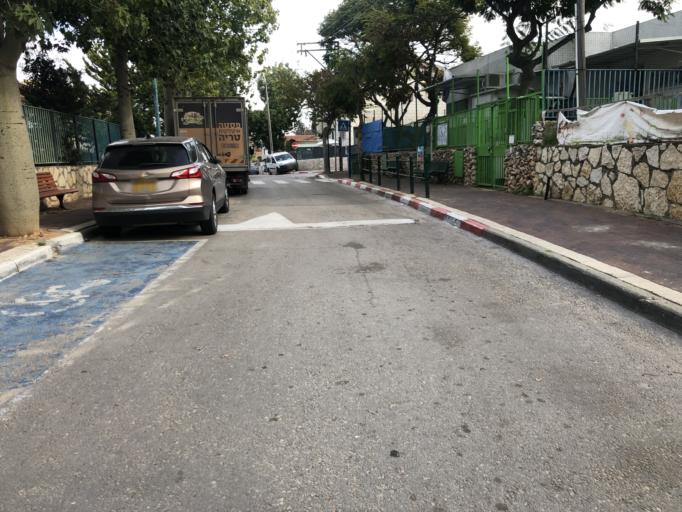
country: IL
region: Central District
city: Kfar Saba
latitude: 32.1895
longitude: 34.8996
